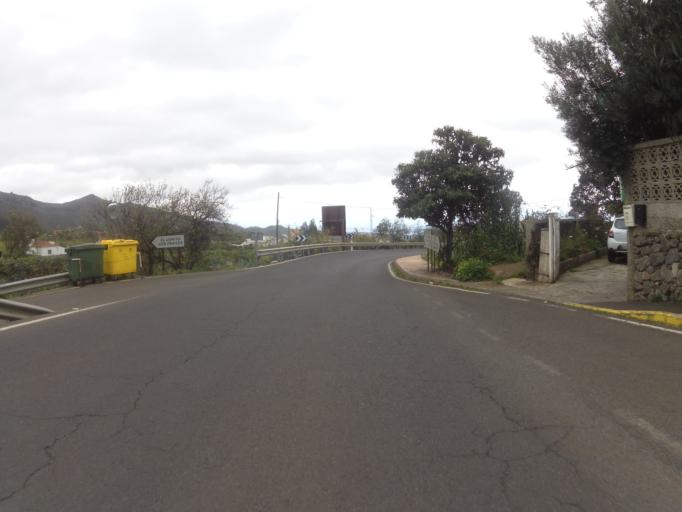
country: ES
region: Canary Islands
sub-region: Provincia de Las Palmas
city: Valsequillo de Gran Canaria
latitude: 27.9854
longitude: -15.5050
